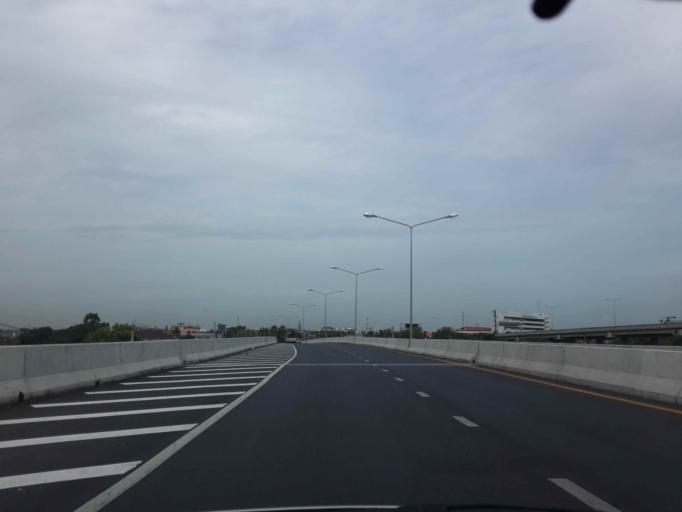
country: TH
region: Bangkok
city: Bang Khen
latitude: 13.8757
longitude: 100.6483
